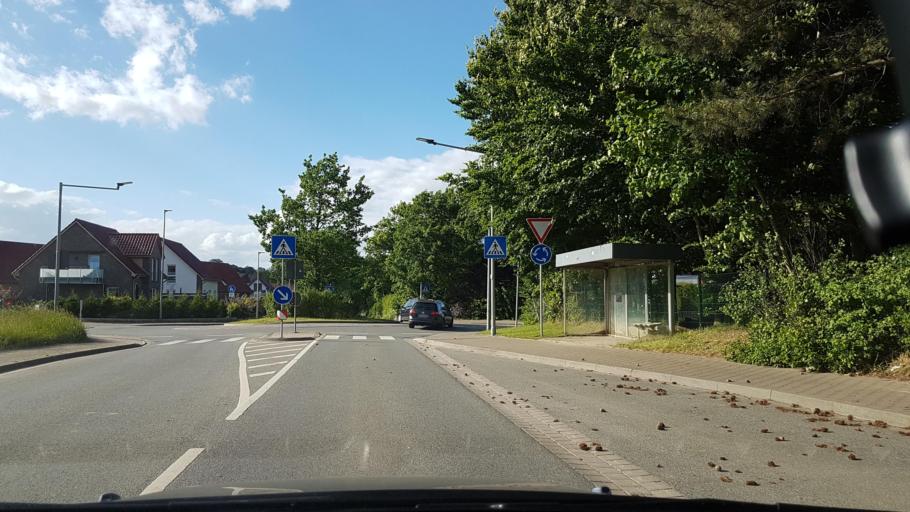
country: DE
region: Lower Saxony
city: Elze
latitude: 52.1669
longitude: 9.6580
